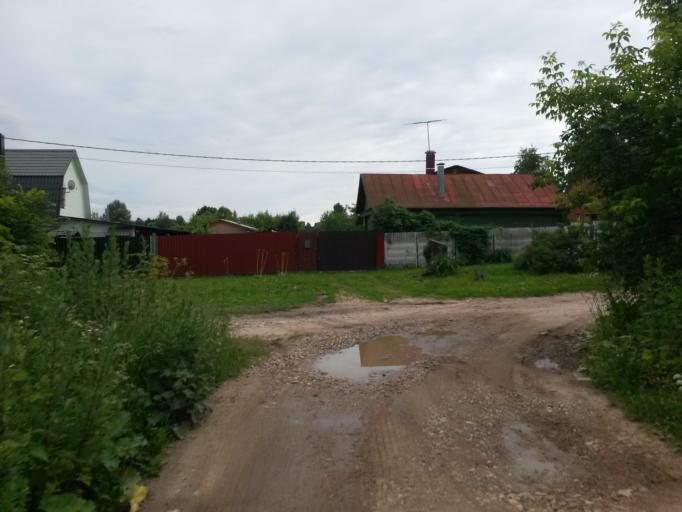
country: RU
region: Moskovskaya
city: Lyubuchany
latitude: 55.2554
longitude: 37.6130
